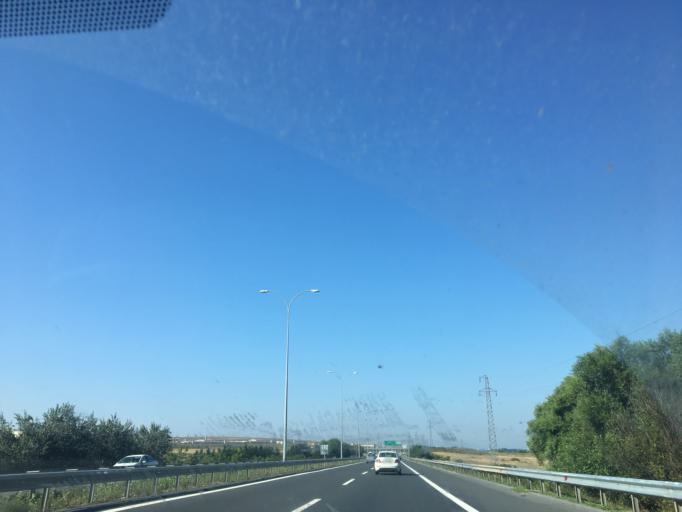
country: TR
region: Istanbul
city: Canta
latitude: 41.1024
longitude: 28.1550
